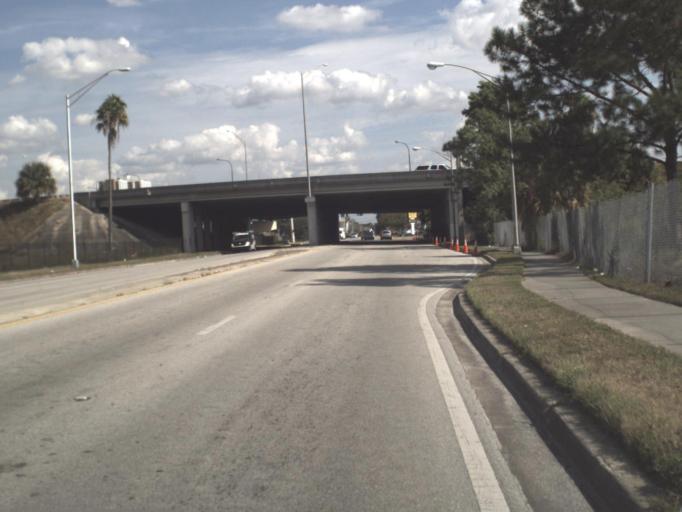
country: US
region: Florida
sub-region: Orange County
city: Orlando
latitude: 28.5310
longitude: -81.3872
